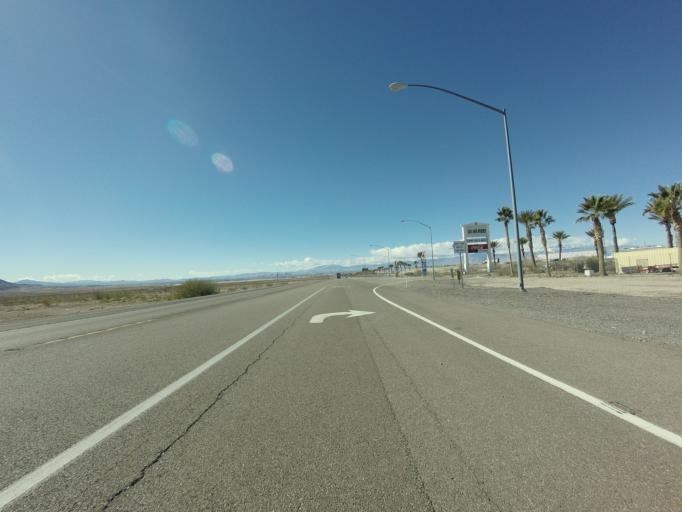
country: US
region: Nevada
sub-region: Clark County
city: Nellis Air Force Base
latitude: 36.2718
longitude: -115.0010
